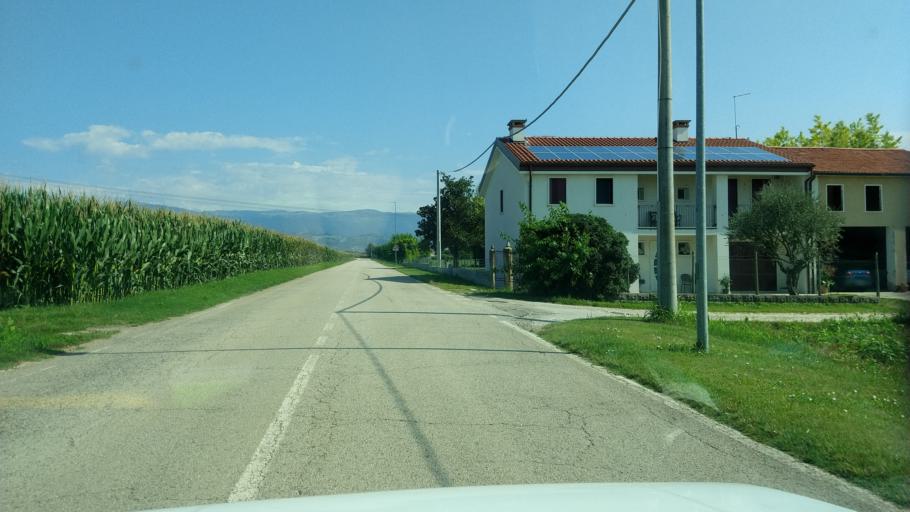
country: IT
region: Veneto
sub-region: Provincia di Vicenza
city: Sandrigo
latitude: 45.6762
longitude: 11.6091
